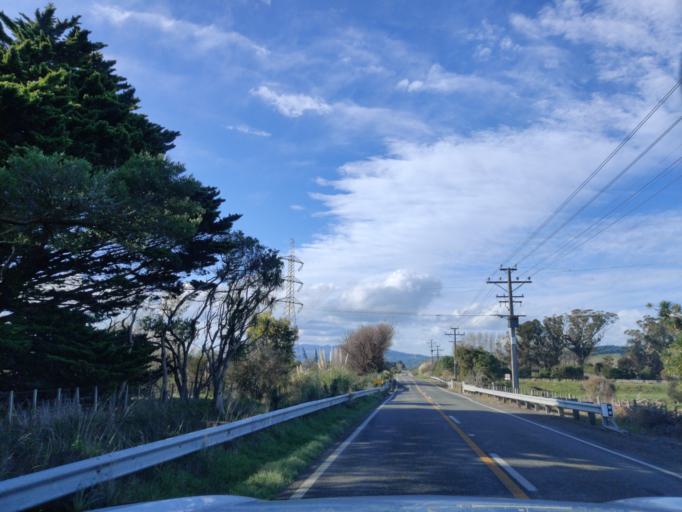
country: NZ
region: Manawatu-Wanganui
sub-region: Palmerston North City
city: Palmerston North
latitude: -40.3445
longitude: 175.7103
